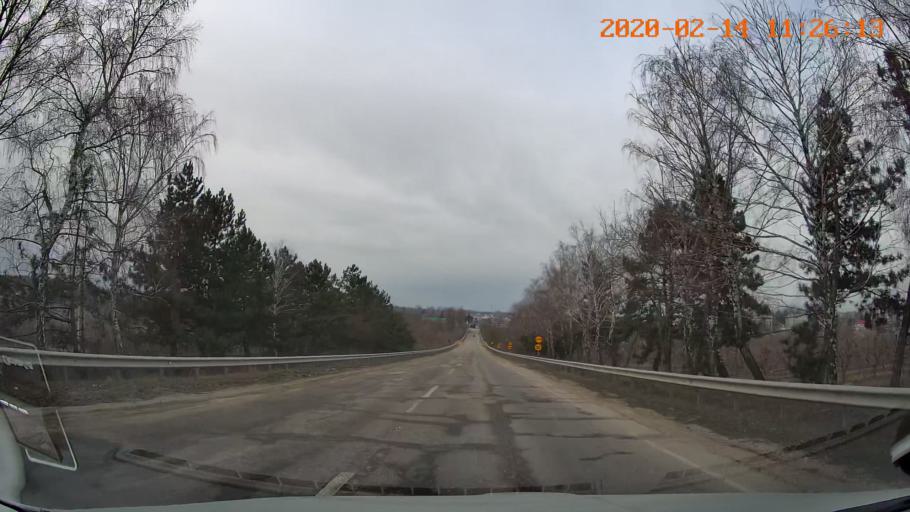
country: MD
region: Briceni
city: Briceni
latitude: 48.3517
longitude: 27.0932
